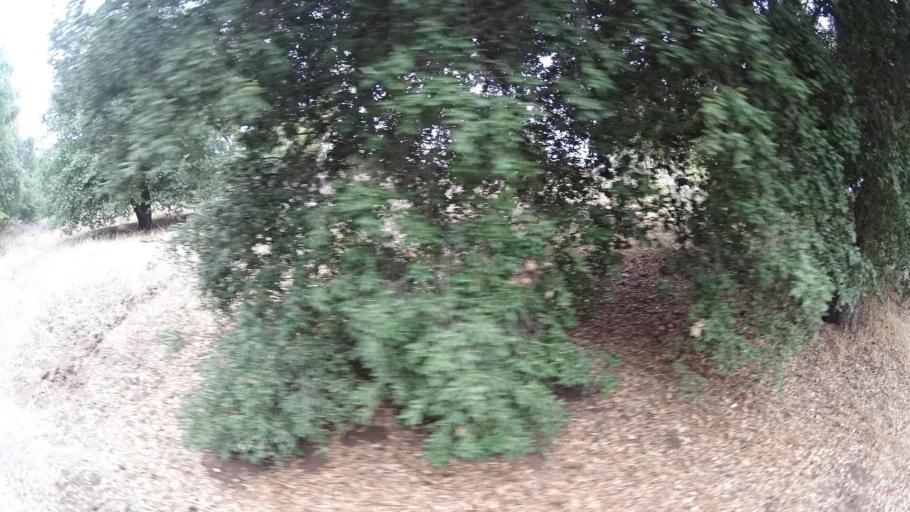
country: US
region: California
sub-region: San Diego County
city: Julian
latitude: 33.0038
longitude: -116.6372
